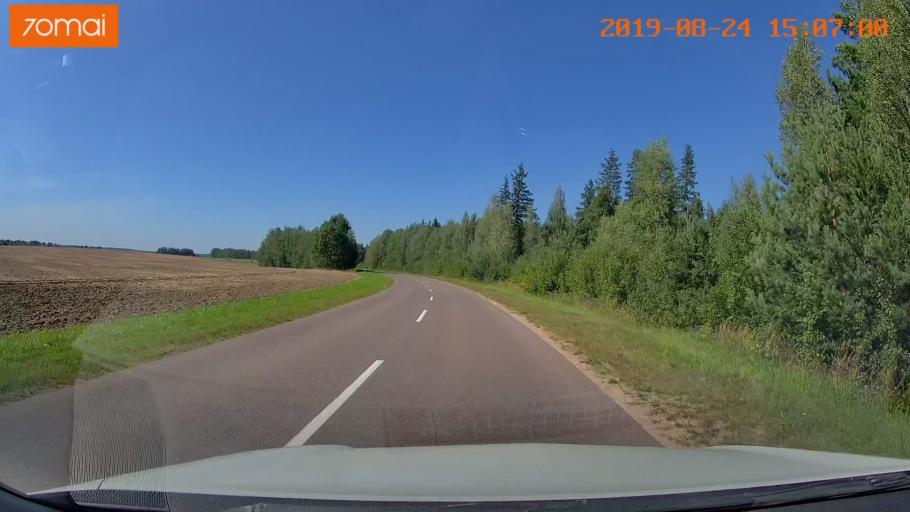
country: BY
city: Michanovichi
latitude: 53.6055
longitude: 27.6781
